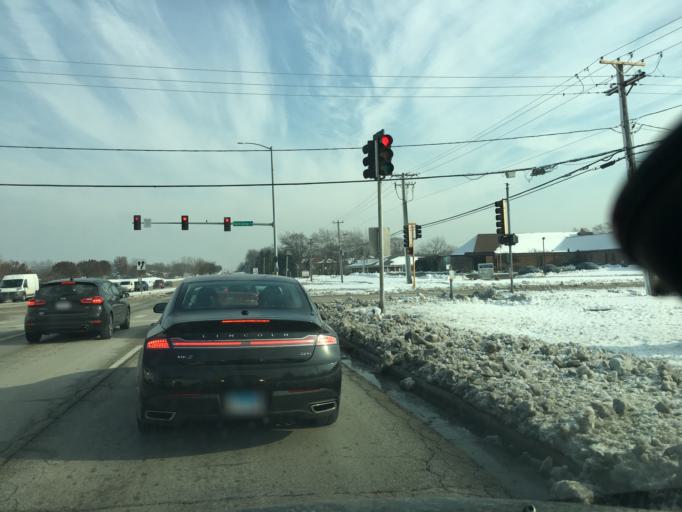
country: US
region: Illinois
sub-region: DuPage County
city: Darien
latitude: 41.7514
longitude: -87.9938
